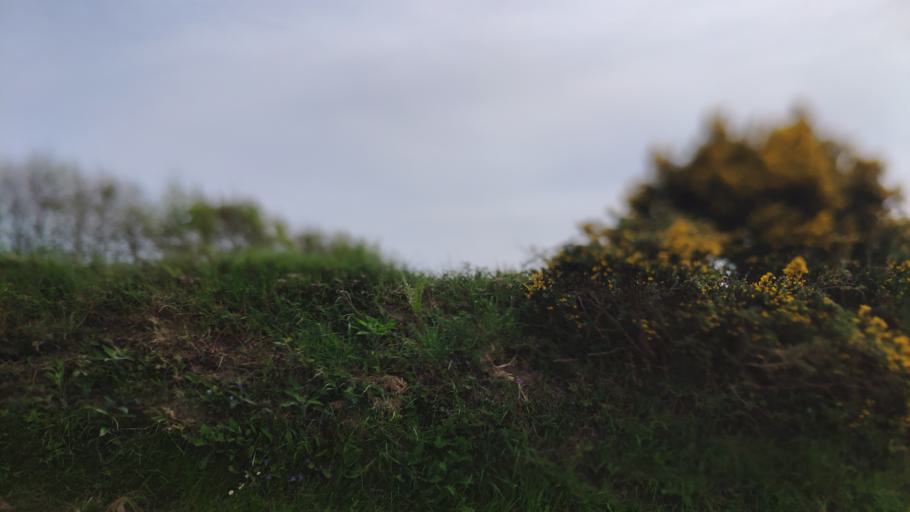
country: IE
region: Munster
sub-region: County Cork
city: Blarney
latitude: 51.9878
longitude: -8.5082
